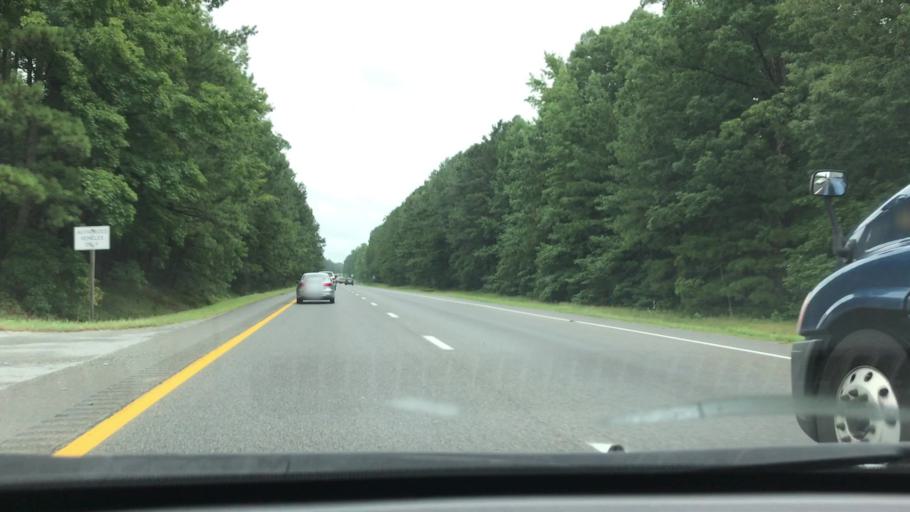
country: US
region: Virginia
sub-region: City of Emporia
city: Emporia
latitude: 36.7386
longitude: -77.5185
